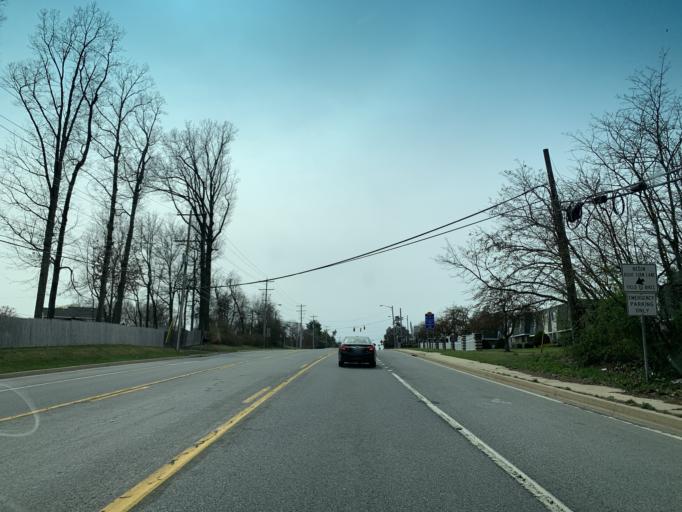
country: US
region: Delaware
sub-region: New Castle County
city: Bear
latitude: 39.6556
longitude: -75.6778
